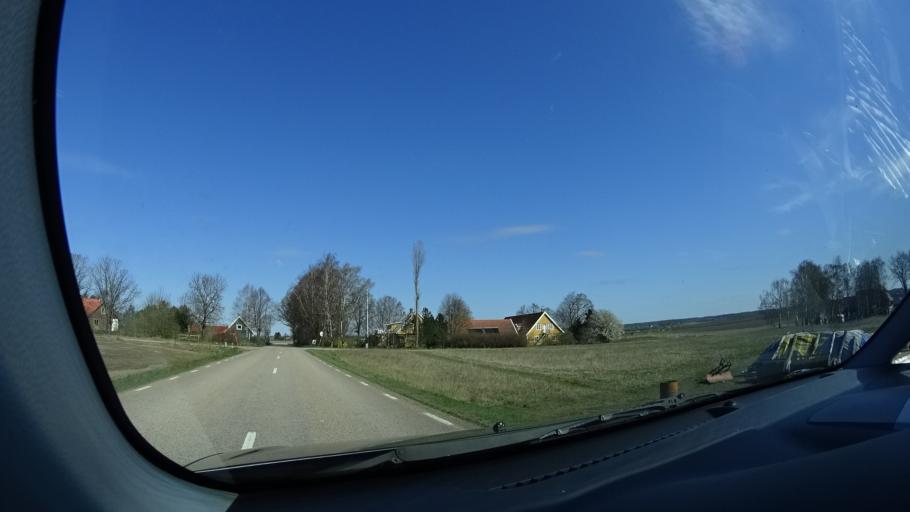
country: SE
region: Skane
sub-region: Astorps Kommun
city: Kvidinge
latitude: 56.1197
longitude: 13.0809
